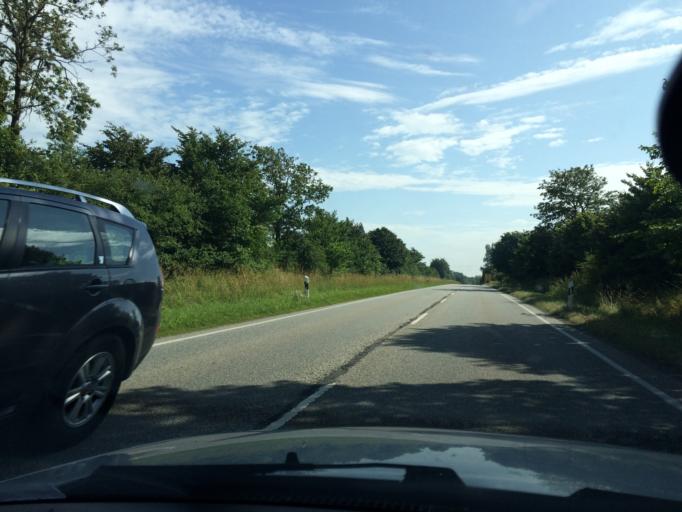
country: DE
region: Schleswig-Holstein
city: Oeversee
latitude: 54.7115
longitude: 9.4397
